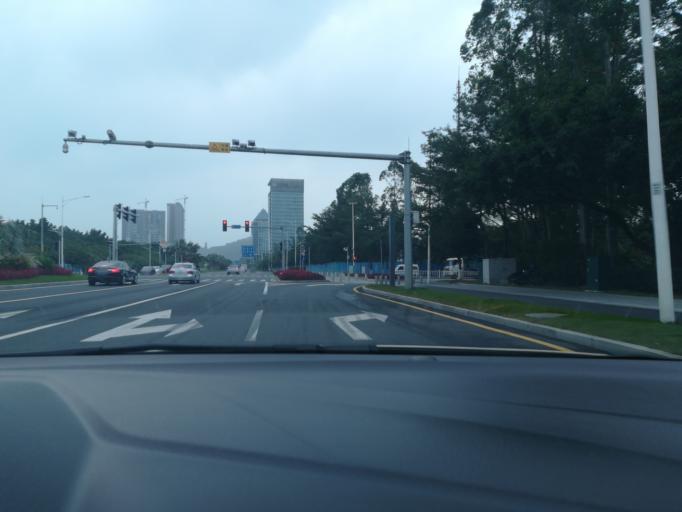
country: CN
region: Guangdong
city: Nansha
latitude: 22.7775
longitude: 113.5967
